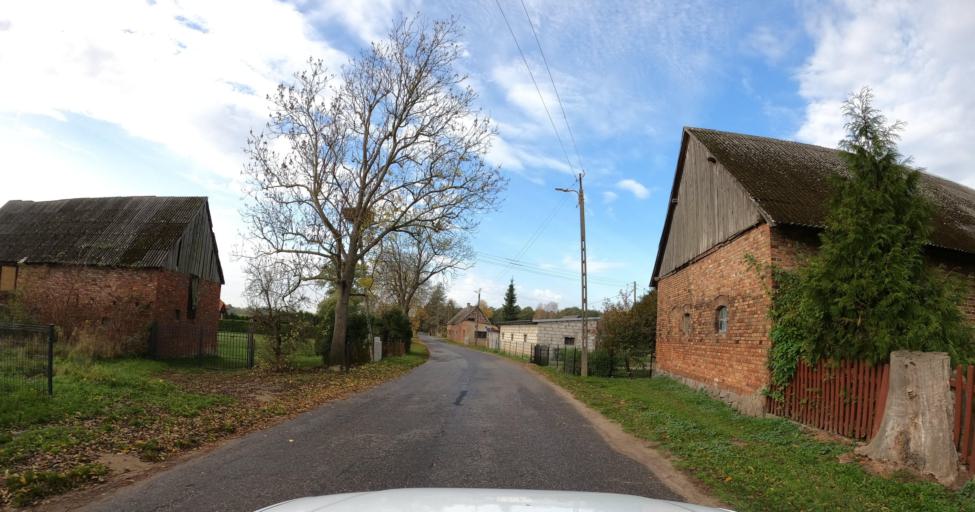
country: PL
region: West Pomeranian Voivodeship
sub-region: Powiat kamienski
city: Kamien Pomorski
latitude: 53.9635
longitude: 14.8296
